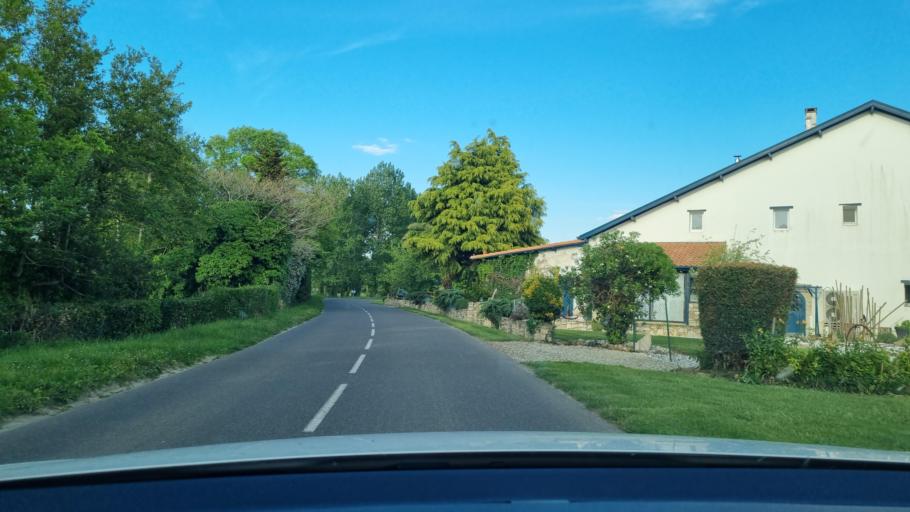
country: FR
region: Aquitaine
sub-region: Departement des Landes
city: Peyrehorade
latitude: 43.5397
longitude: -1.1203
